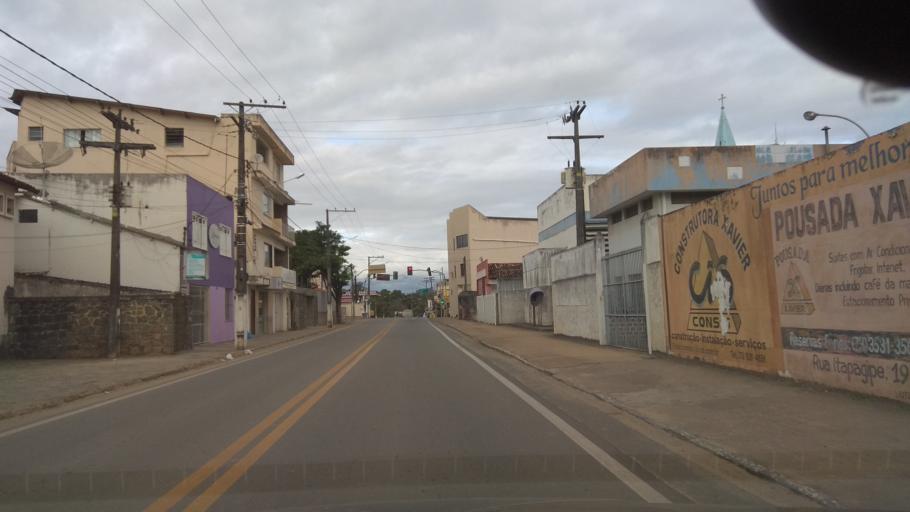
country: BR
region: Bahia
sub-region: Ipiau
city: Ipiau
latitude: -14.1377
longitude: -39.7349
